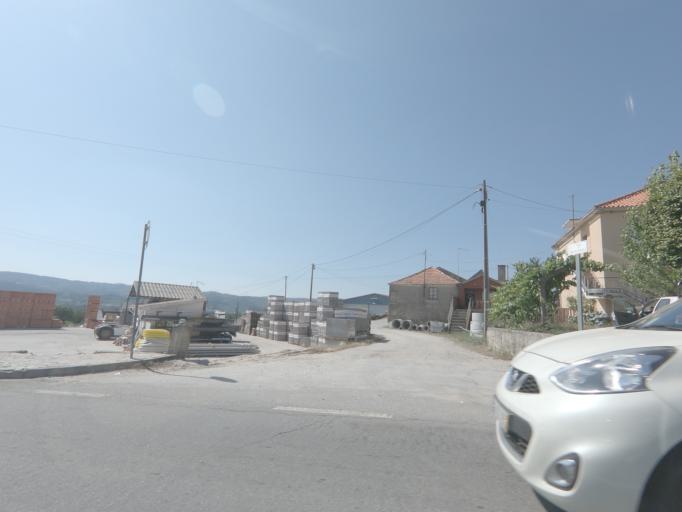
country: PT
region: Viseu
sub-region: Moimenta da Beira
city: Moimenta da Beira
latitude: 40.9869
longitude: -7.6235
